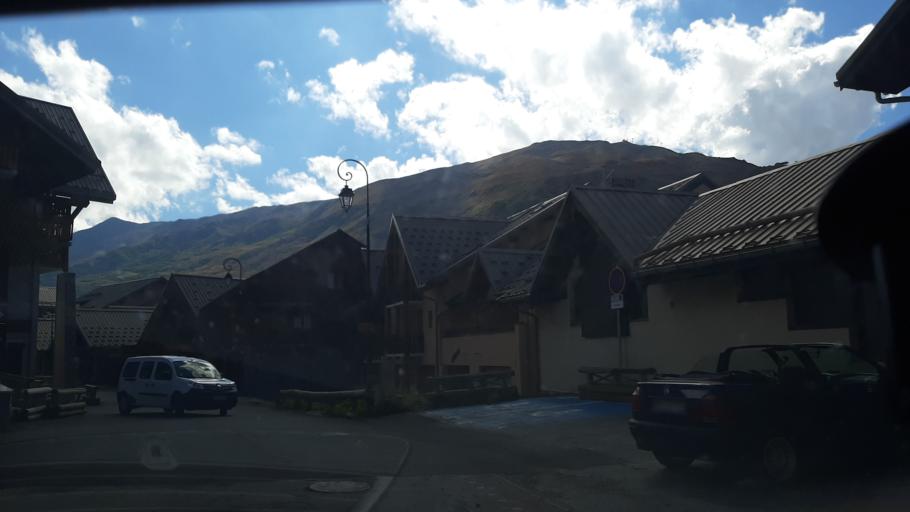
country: FR
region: Rhone-Alpes
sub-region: Departement de la Savoie
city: Saint-Michel-de-Maurienne
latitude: 45.1749
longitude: 6.4933
